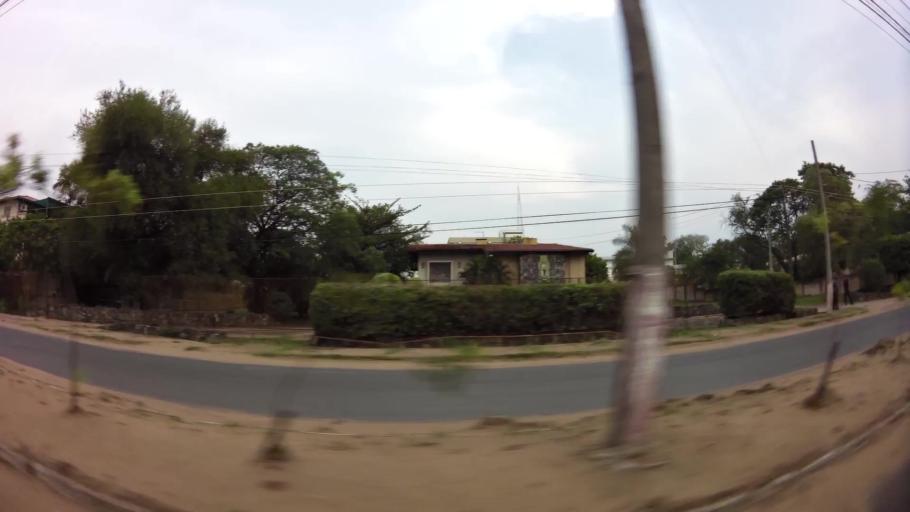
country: PY
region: Central
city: Lambare
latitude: -25.3569
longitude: -57.6440
